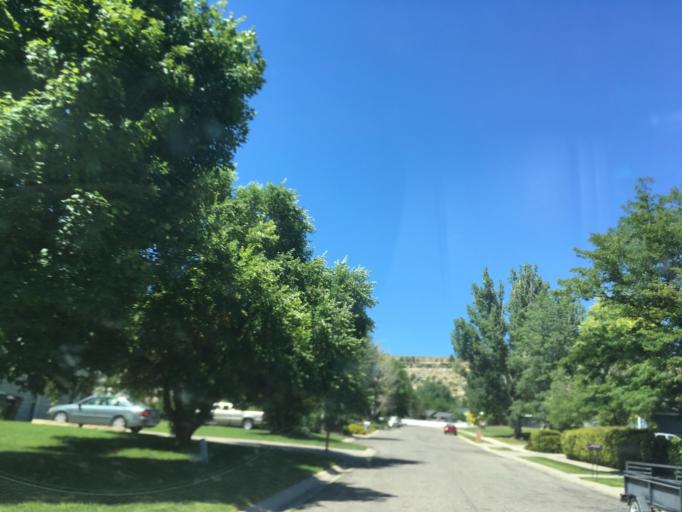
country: US
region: Montana
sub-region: Yellowstone County
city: Billings
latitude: 45.7964
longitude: -108.5618
